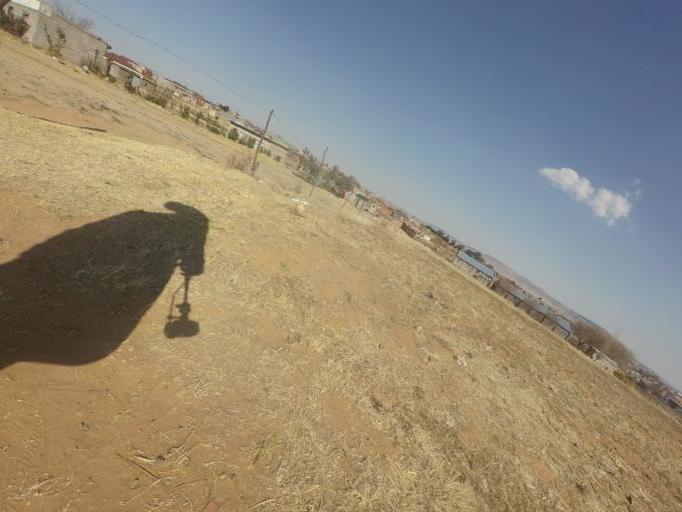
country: LS
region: Leribe
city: Maputsoe
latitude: -28.8967
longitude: 27.9192
